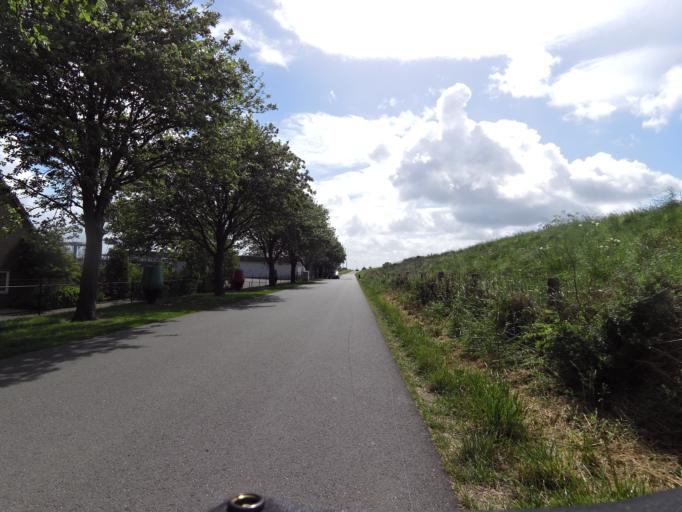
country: NL
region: Zeeland
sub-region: Schouwen-Duiveland
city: Bruinisse
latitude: 51.6694
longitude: 4.0832
